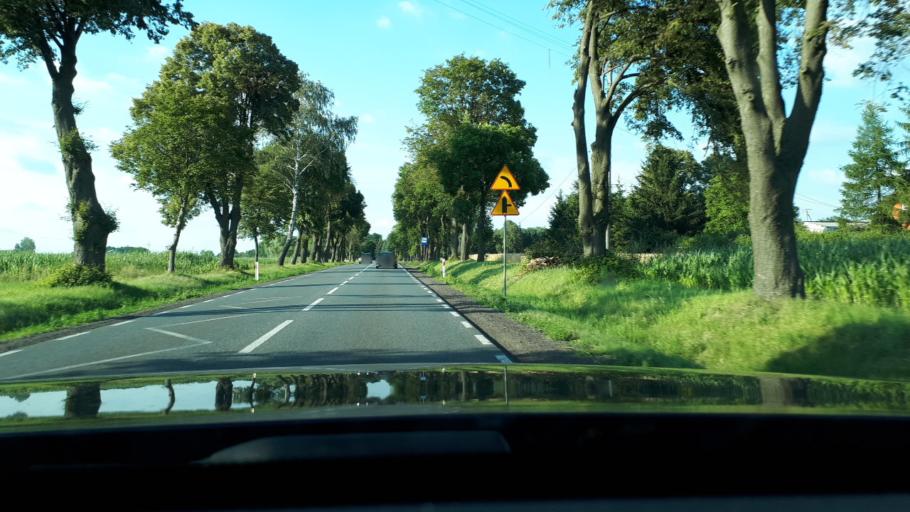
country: PL
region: Masovian Voivodeship
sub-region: Powiat ciechanowski
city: Ciechanow
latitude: 52.8253
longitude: 20.6166
